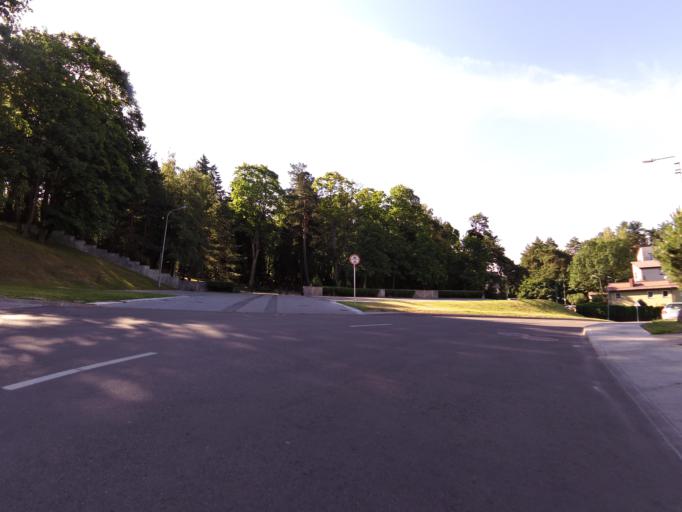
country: LT
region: Vilnius County
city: Rasos
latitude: 54.6993
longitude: 25.3175
